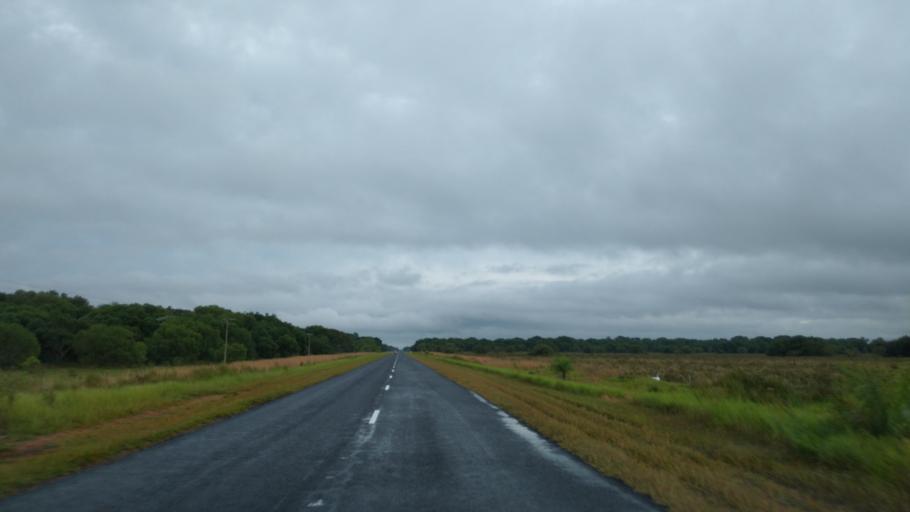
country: AR
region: Corrientes
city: Loreto
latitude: -27.7530
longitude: -57.2572
